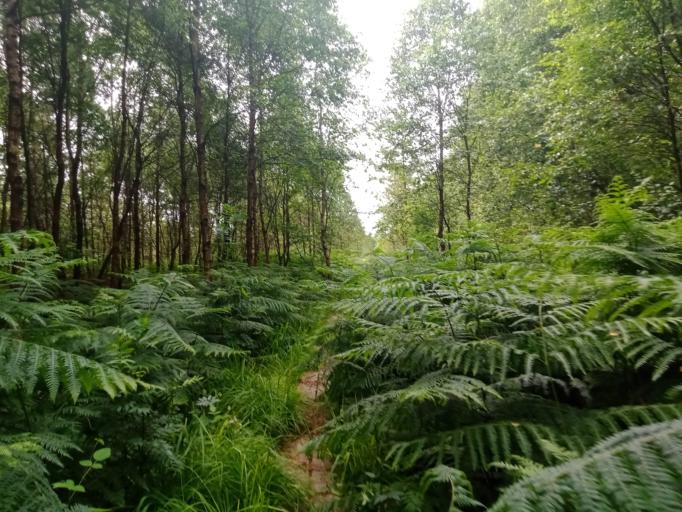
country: IE
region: Leinster
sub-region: Laois
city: Abbeyleix
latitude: 52.8890
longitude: -7.3598
